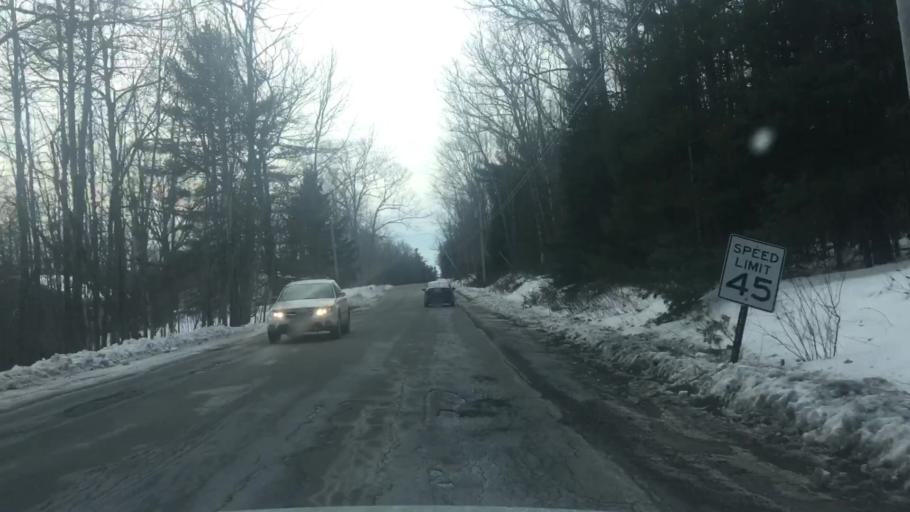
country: US
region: Maine
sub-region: Hancock County
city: Orland
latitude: 44.6101
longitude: -68.7143
